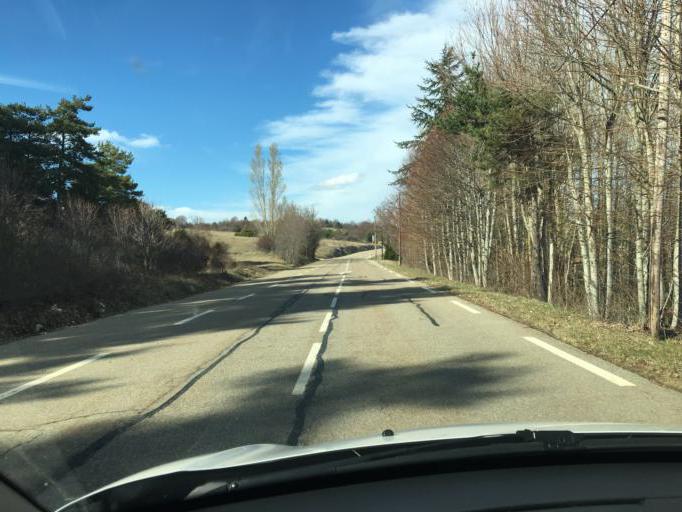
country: FR
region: Provence-Alpes-Cote d'Azur
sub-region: Departement du Vaucluse
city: Saint-Saturnin-les-Apt
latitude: 43.9824
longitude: 5.4726
